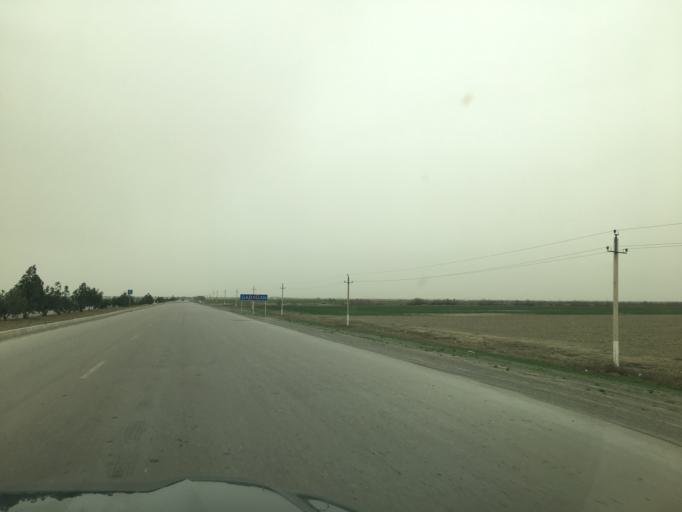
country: TM
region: Ahal
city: Baharly
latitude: 38.3833
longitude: 57.4978
